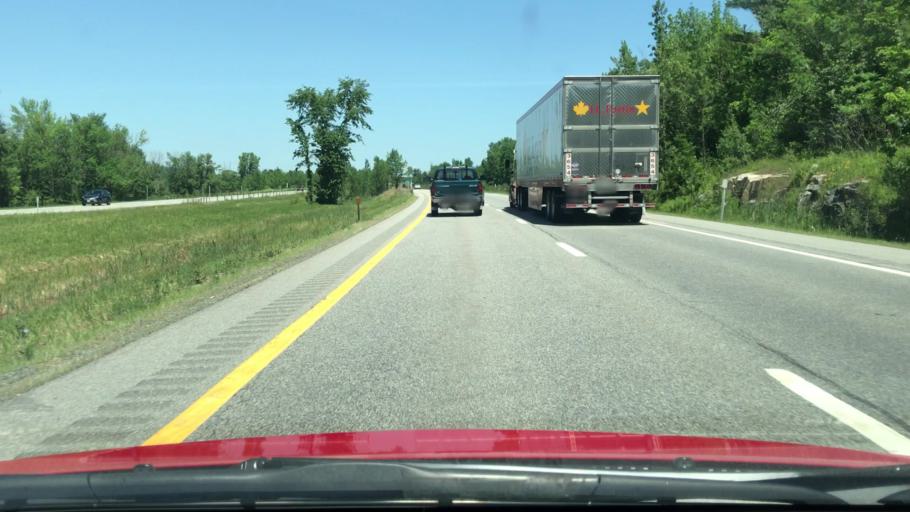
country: US
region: New York
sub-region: Essex County
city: Keeseville
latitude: 44.4301
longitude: -73.4913
